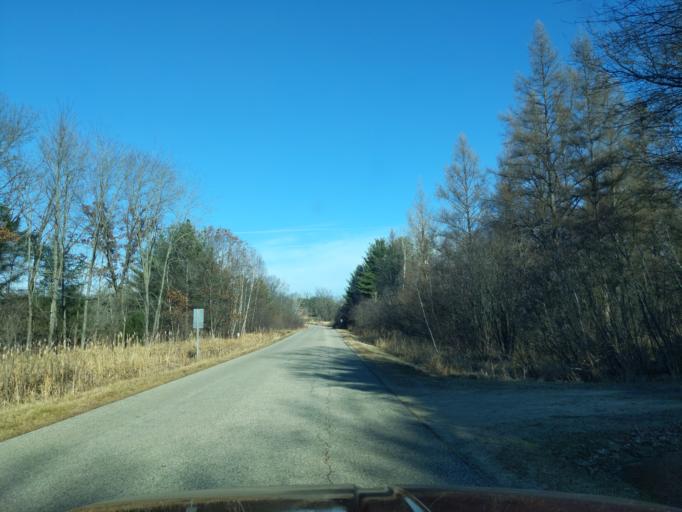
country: US
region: Wisconsin
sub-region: Waushara County
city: Silver Lake
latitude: 44.0602
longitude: -89.1887
